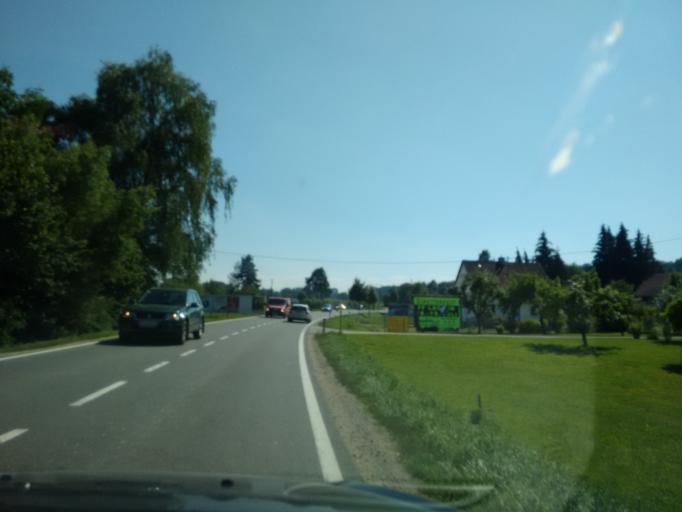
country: AT
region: Upper Austria
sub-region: Wels-Land
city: Buchkirchen
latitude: 48.2601
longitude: 13.9768
